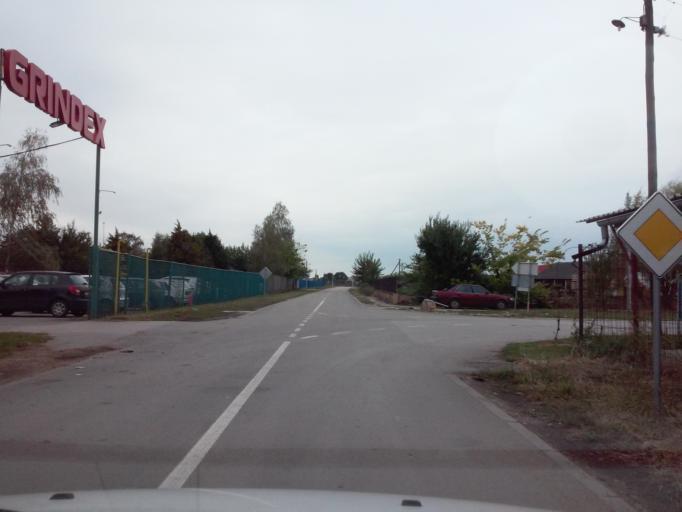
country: RS
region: Autonomna Pokrajina Vojvodina
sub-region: Severnobanatski Okrug
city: Kikinda
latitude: 45.8200
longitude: 20.4774
